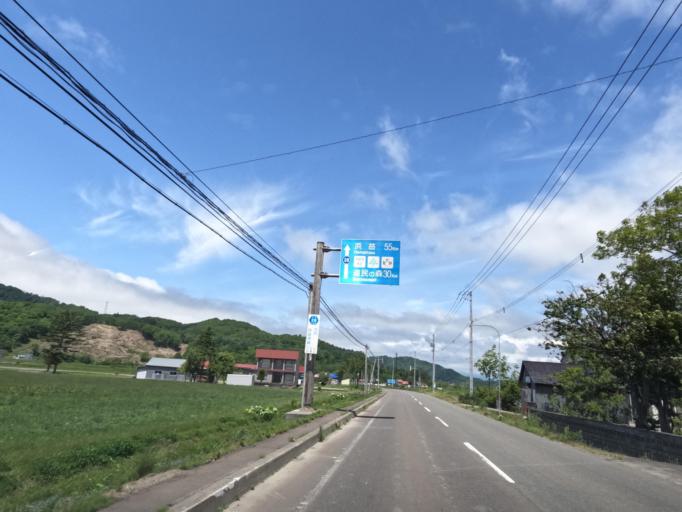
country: JP
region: Hokkaido
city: Tobetsu
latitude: 43.2917
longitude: 141.5393
